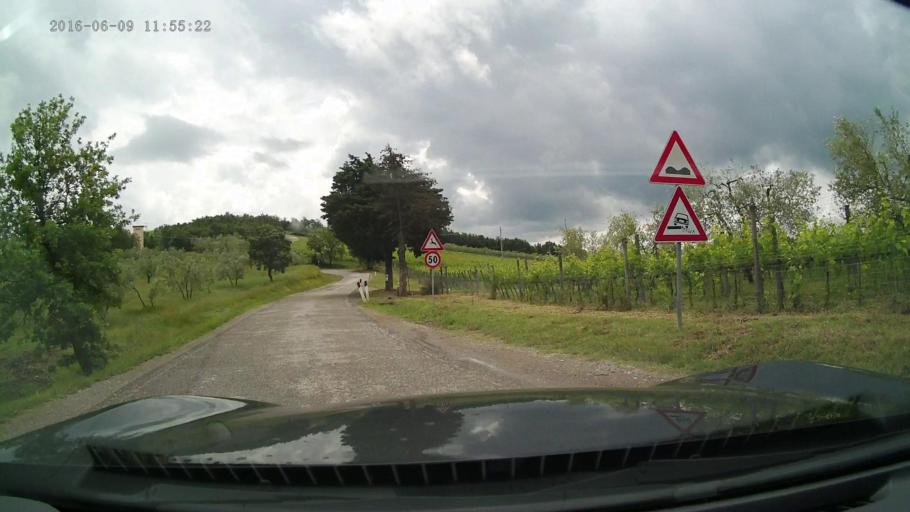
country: IT
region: Tuscany
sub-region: Province of Florence
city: Panzano in Chianti
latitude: 43.5651
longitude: 11.2904
